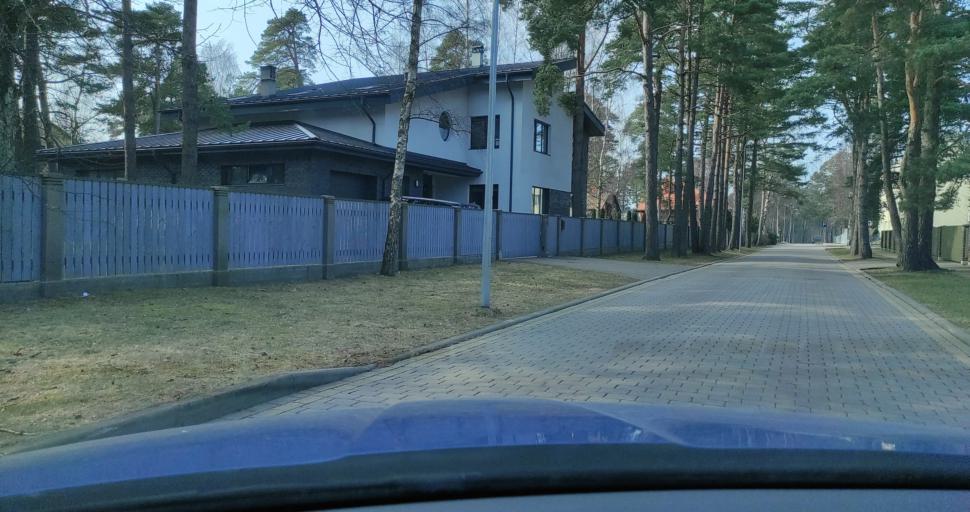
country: LV
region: Ventspils
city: Ventspils
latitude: 57.3846
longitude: 21.5431
